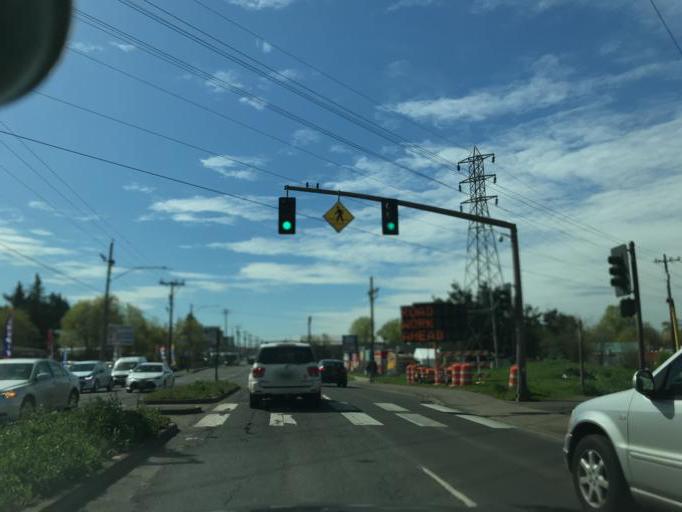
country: US
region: Oregon
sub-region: Multnomah County
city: Lents
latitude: 45.4645
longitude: -122.5791
